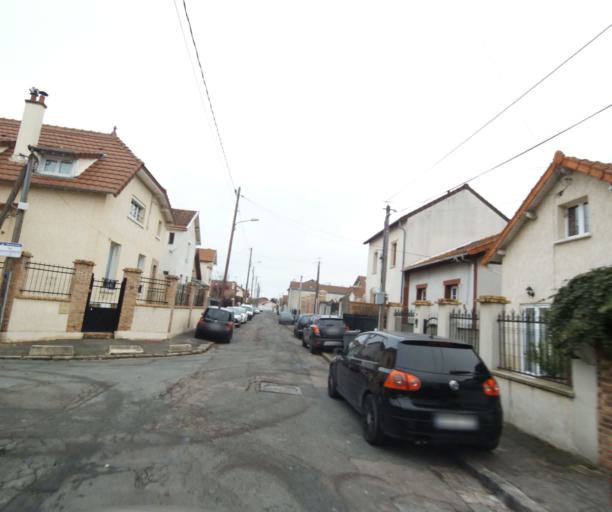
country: FR
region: Ile-de-France
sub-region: Departement du Val-de-Marne
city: Ablon-sur-Seine
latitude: 48.7293
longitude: 2.4234
